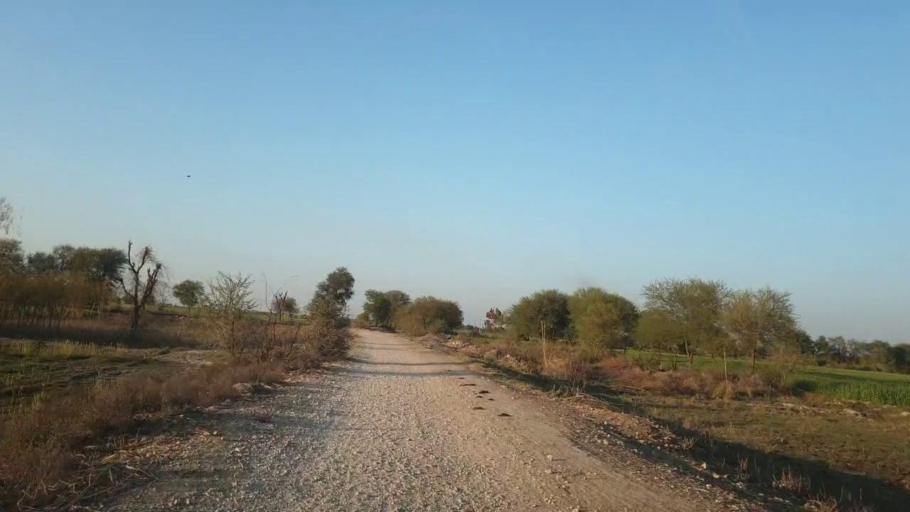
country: PK
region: Sindh
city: Mirpur Khas
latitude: 25.6934
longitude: 69.0508
